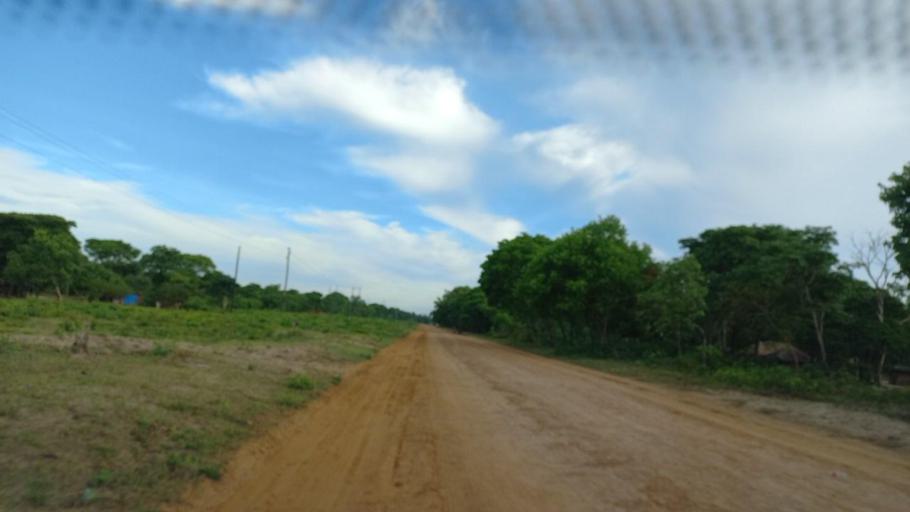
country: ZM
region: North-Western
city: Kabompo
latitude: -13.4083
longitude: 24.3140
